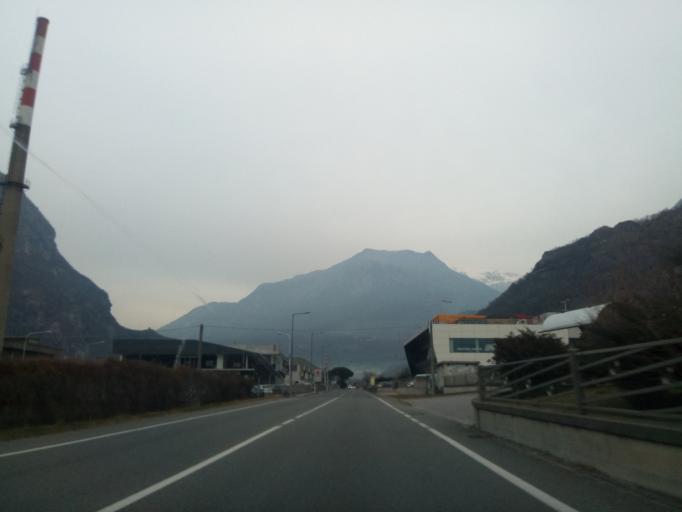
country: IT
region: Piedmont
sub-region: Provincia di Torino
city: Quincinetto
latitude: 45.5678
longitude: 7.8132
